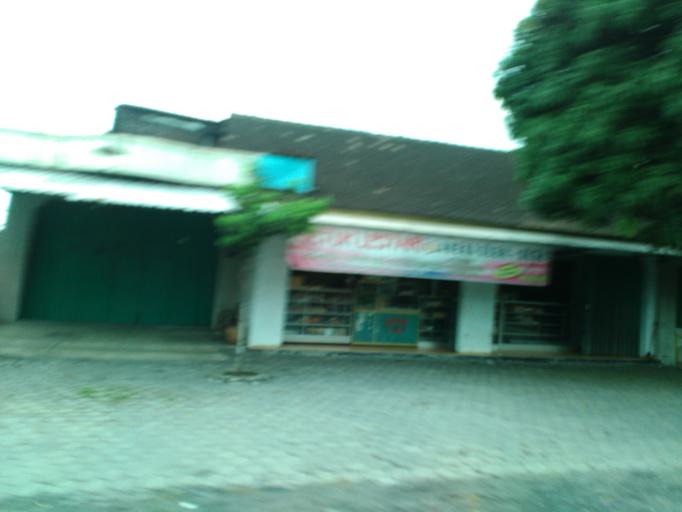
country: ID
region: Central Java
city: Gatak
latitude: -7.5931
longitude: 110.7027
